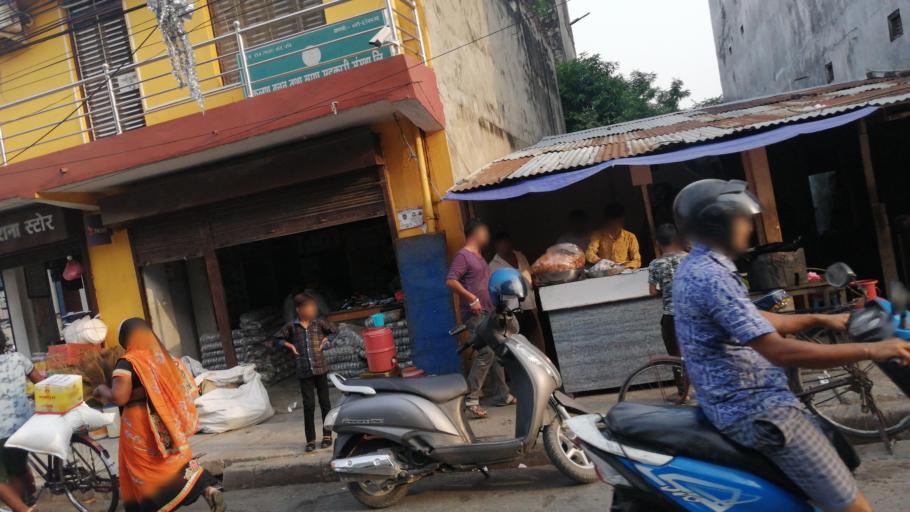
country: NP
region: Western Region
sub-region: Lumbini Zone
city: Bhairahawa
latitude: 27.5067
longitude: 83.4490
